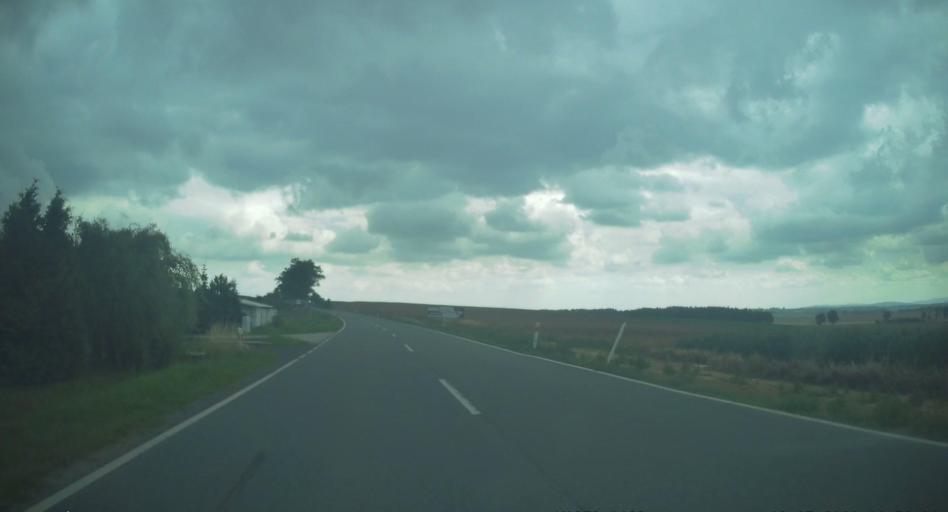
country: PL
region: Opole Voivodeship
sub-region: Powiat nyski
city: Nysa
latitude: 50.4234
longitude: 17.4396
